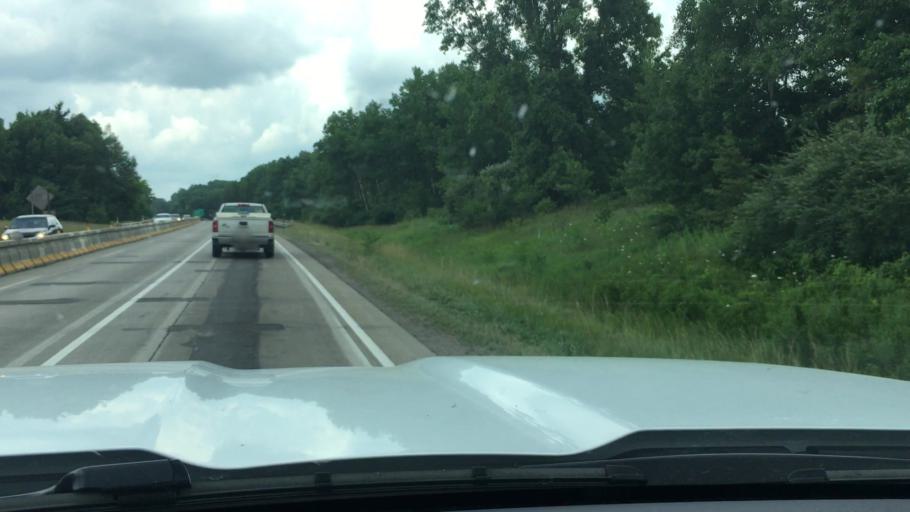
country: US
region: Michigan
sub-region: Kent County
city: Rockford
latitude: 43.1631
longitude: -85.5761
